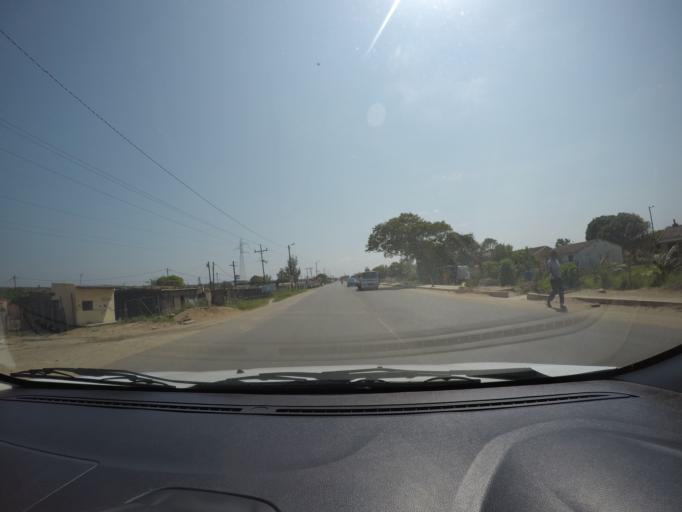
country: ZA
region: KwaZulu-Natal
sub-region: uThungulu District Municipality
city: eSikhawini
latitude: -28.8701
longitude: 31.9020
